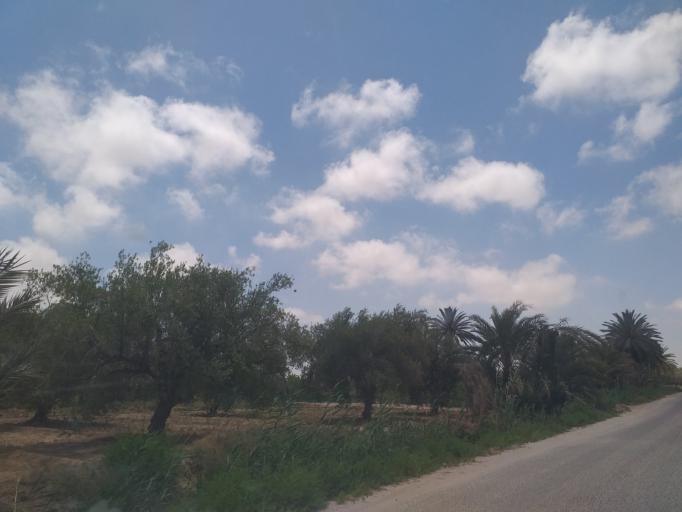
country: TN
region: Qabis
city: Gabes
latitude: 33.9309
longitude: 10.0547
